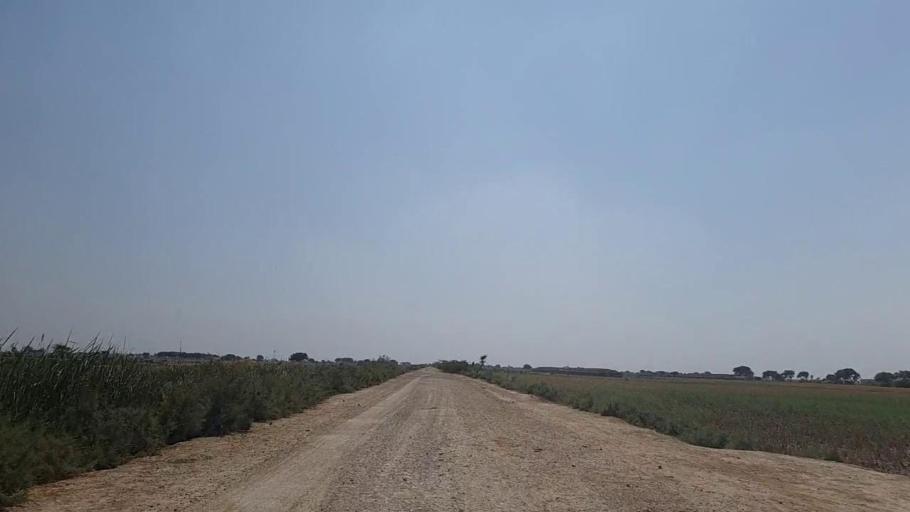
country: PK
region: Sindh
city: Mirpur Batoro
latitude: 24.5482
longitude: 68.3168
